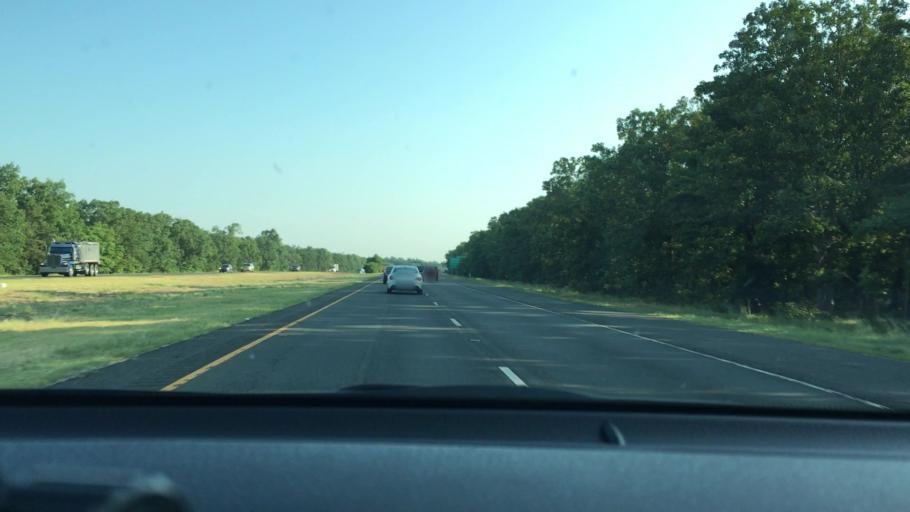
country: US
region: New Jersey
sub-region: Cumberland County
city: Vineland
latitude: 39.5135
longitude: -75.0694
